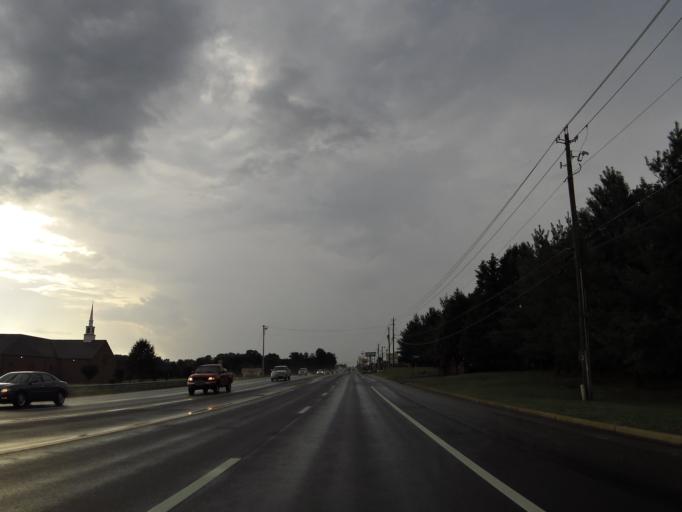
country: US
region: Tennessee
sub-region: Sevier County
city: Seymour
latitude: 35.8656
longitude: -83.7487
